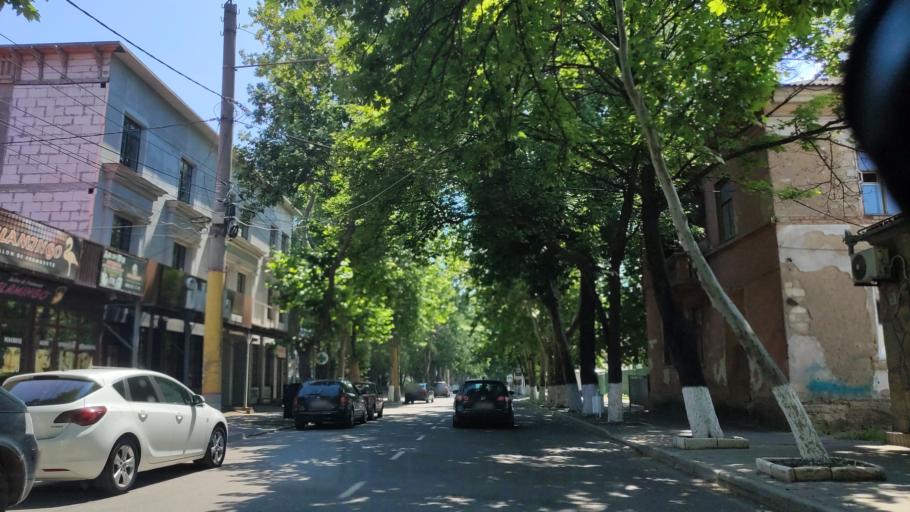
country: MD
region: Raionul Soroca
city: Soroca
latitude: 48.1561
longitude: 28.3001
